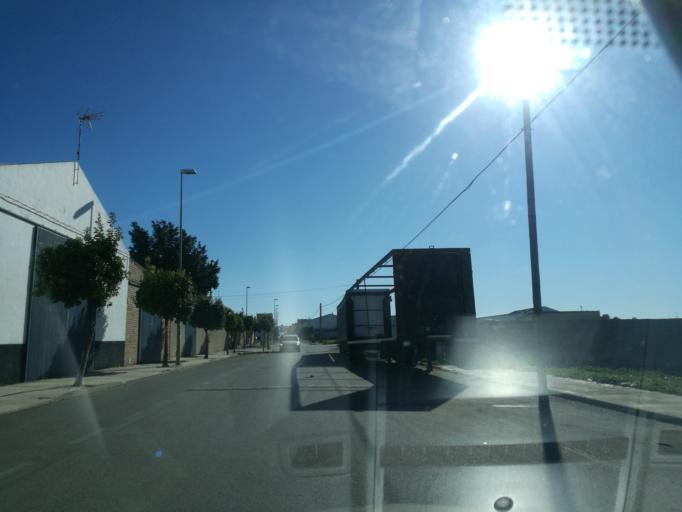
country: ES
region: Andalusia
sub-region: Provincia de Sevilla
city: La Campana
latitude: 37.5743
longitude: -5.4310
